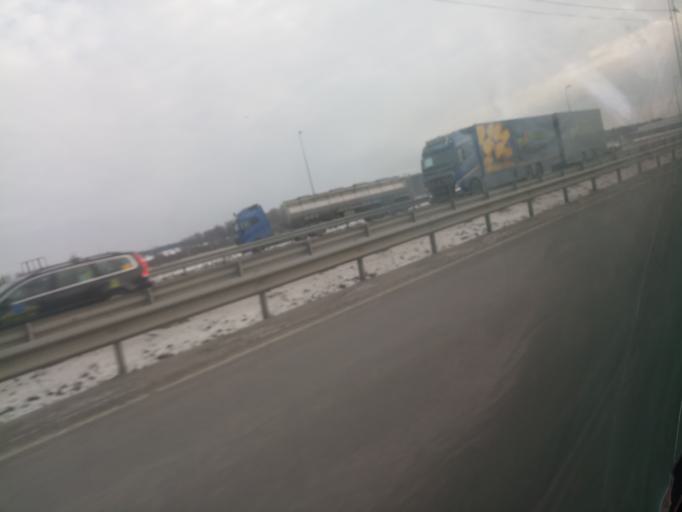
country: SE
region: Stockholm
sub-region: Sigtuna Kommun
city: Rosersberg
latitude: 59.5756
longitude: 17.8999
